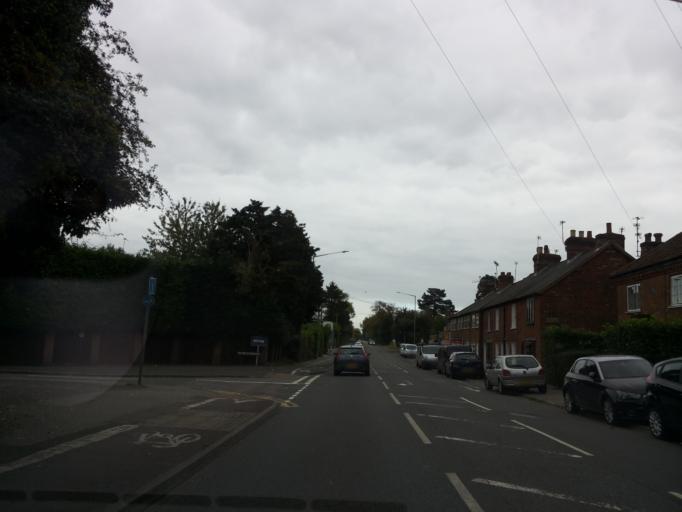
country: GB
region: England
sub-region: Buckinghamshire
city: Little Chalfont
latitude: 51.6716
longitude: -0.5849
